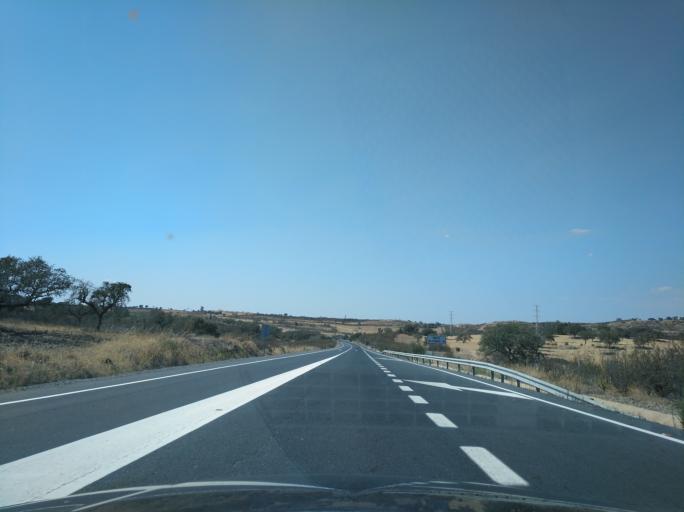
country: ES
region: Andalusia
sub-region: Provincia de Huelva
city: San Bartolome de la Torre
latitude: 37.4682
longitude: -7.1234
